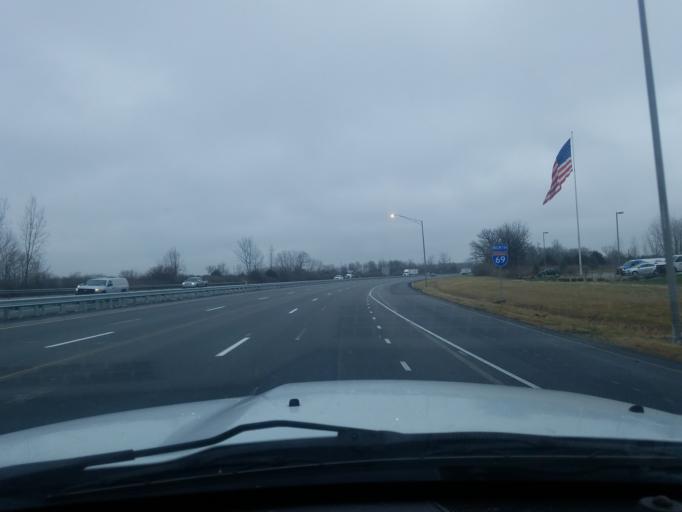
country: US
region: Indiana
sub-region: Hamilton County
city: Fishers
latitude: 39.9658
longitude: -85.9999
